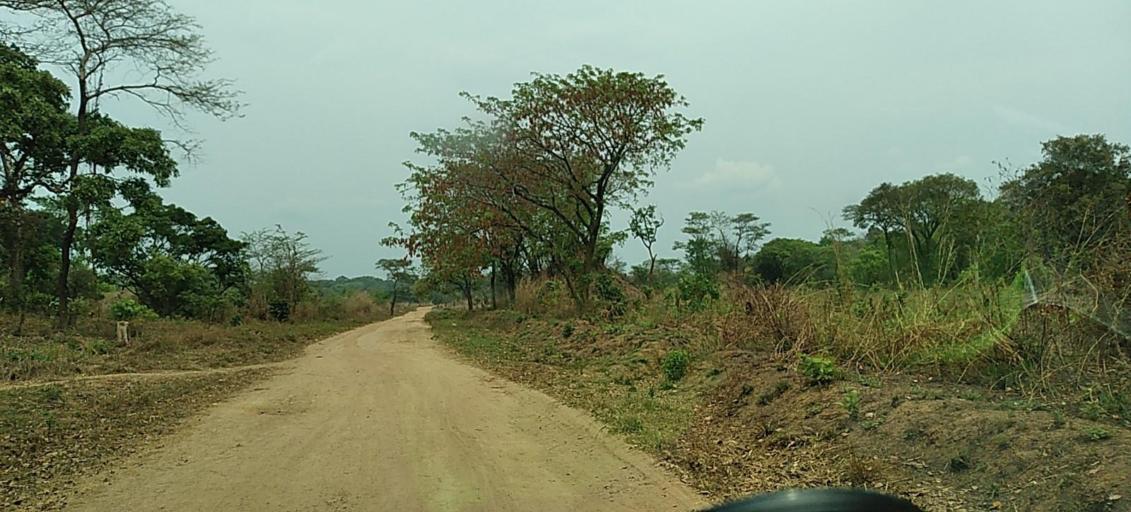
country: ZM
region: North-Western
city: Solwezi
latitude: -12.7913
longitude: 26.5302
